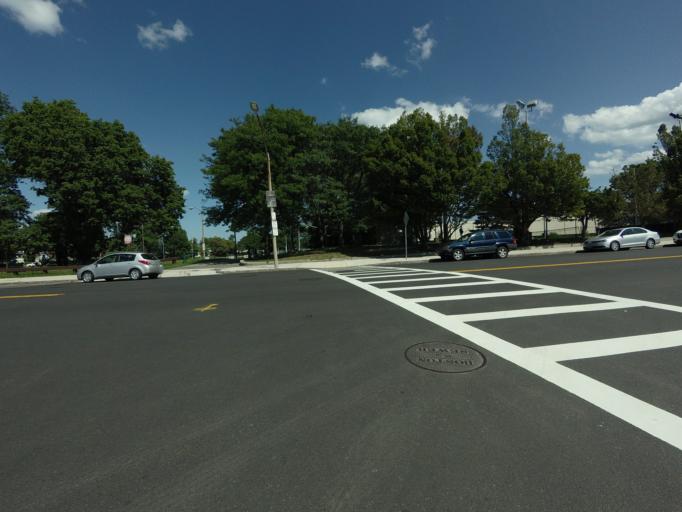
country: US
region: Massachusetts
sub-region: Suffolk County
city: South Boston
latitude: 42.3375
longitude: -71.0252
